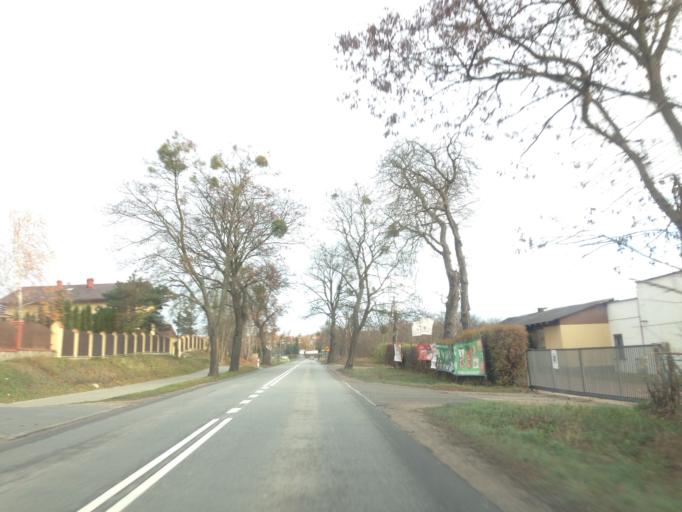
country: PL
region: Pomeranian Voivodeship
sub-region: Powiat gdanski
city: Lublewo Gdanskie
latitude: 54.2859
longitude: 18.5056
